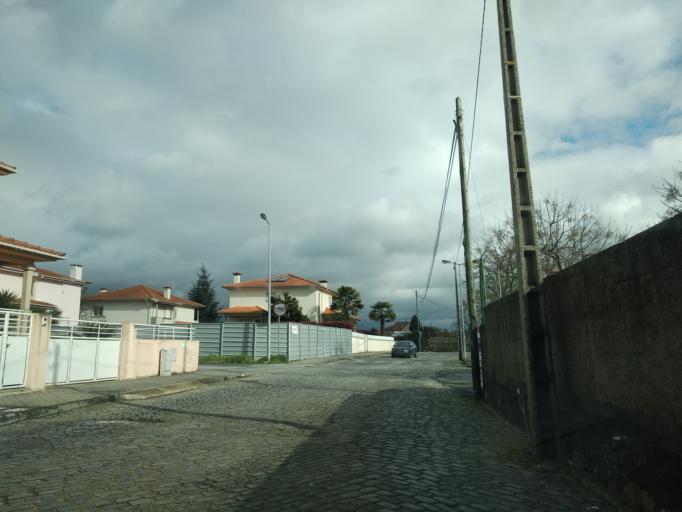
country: PT
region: Braga
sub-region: Braga
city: Braga
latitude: 41.5556
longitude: -8.4452
